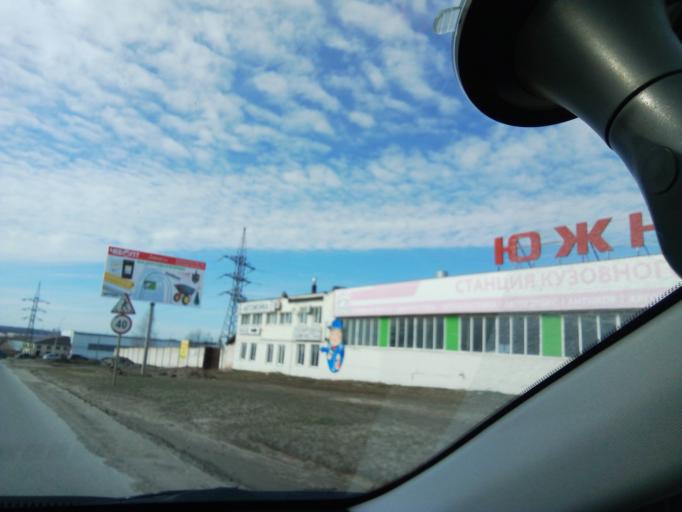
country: RU
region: Chuvashia
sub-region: Cheboksarskiy Rayon
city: Cheboksary
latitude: 56.0997
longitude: 47.2539
